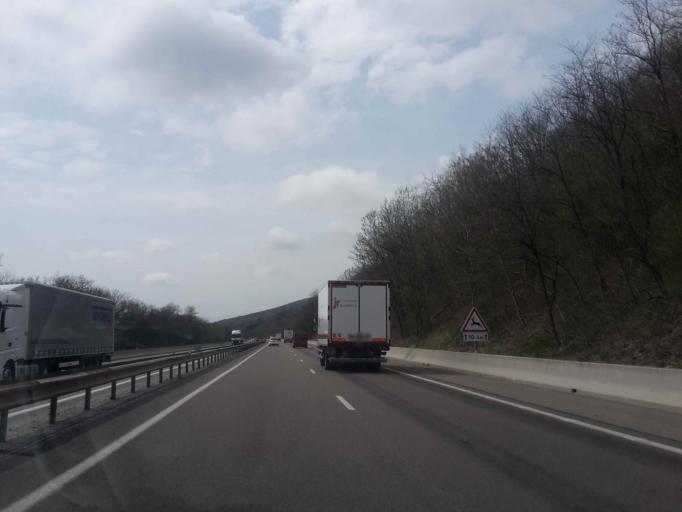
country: FR
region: Franche-Comte
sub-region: Departement du Doubs
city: Thise
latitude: 47.3184
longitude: 6.0914
